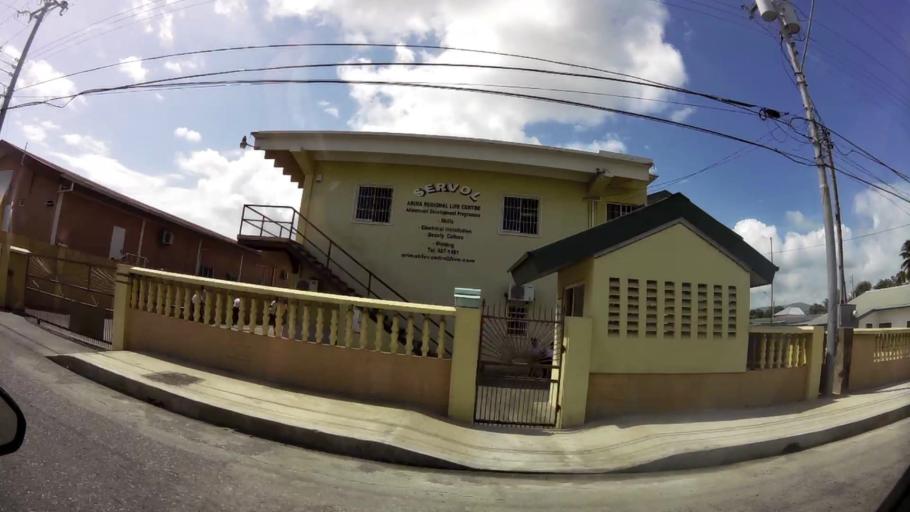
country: TT
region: Borough of Arima
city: Arima
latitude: 10.6279
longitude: -61.2816
